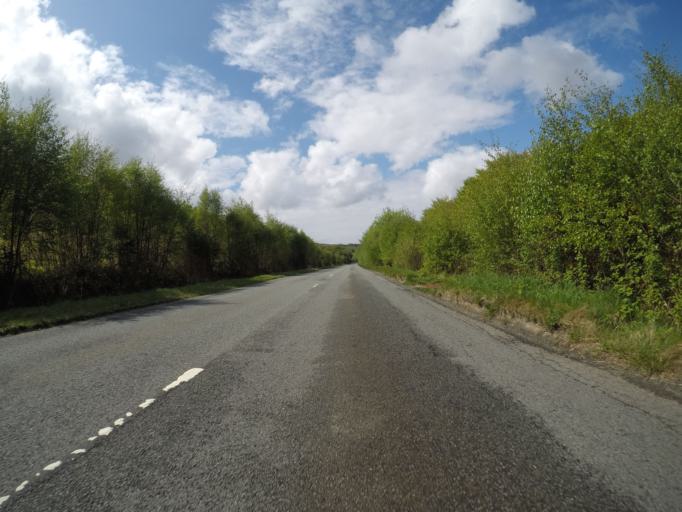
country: GB
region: Scotland
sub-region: Highland
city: Isle of Skye
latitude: 57.4536
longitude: -6.3148
